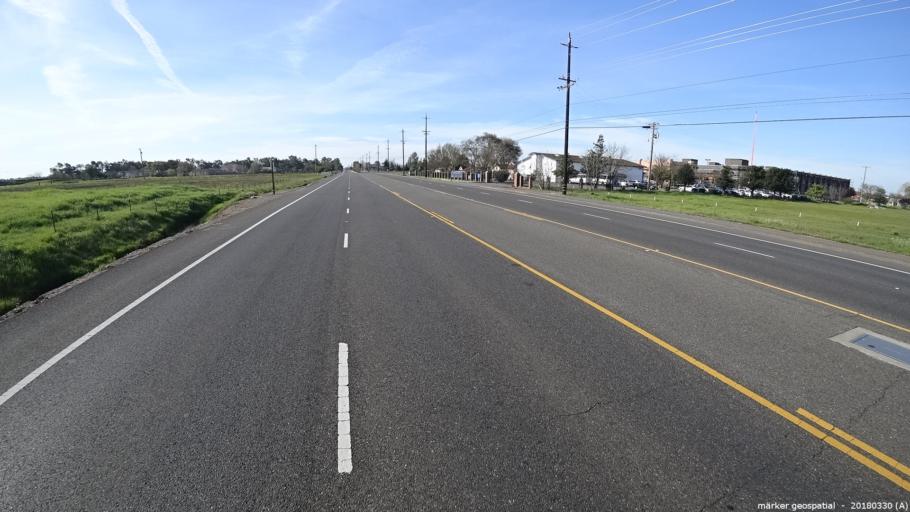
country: US
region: California
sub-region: Sacramento County
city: Vineyard
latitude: 38.4803
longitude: -121.3349
